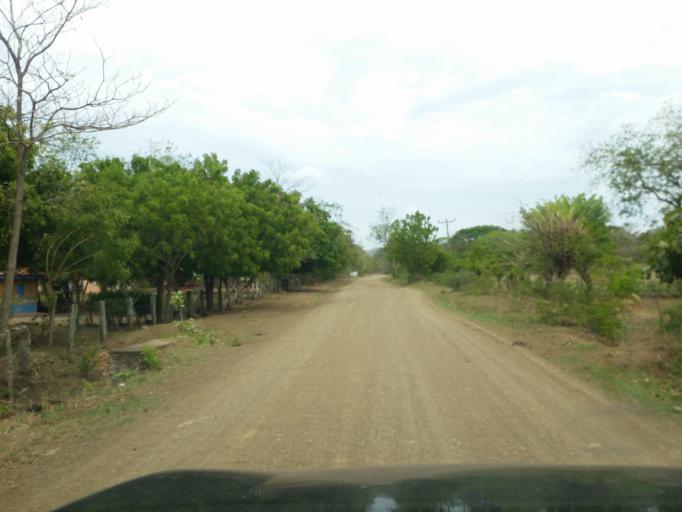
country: NI
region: Granada
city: Nandaime
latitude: 11.6180
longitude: -86.0279
